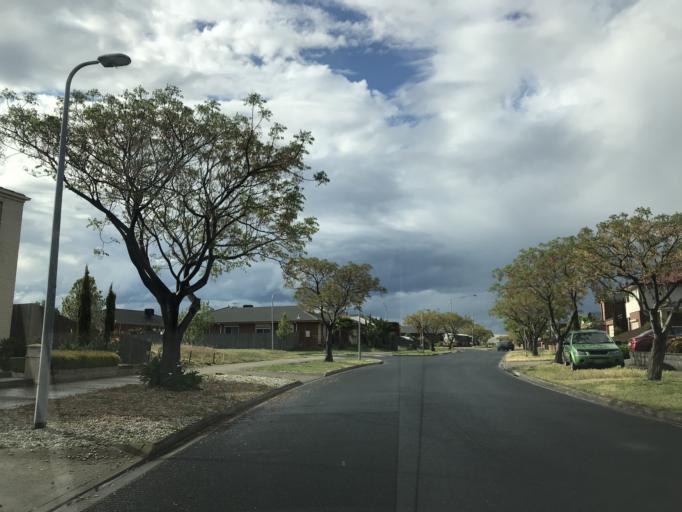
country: AU
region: Victoria
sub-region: Brimbank
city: Derrimut
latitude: -37.7882
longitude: 144.7706
